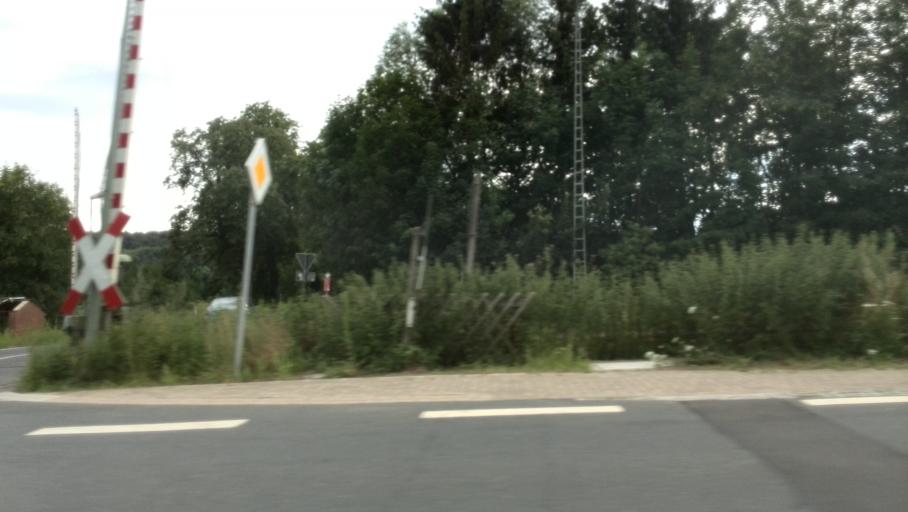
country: DE
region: Lower Saxony
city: Holle
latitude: 52.0987
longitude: 10.1370
